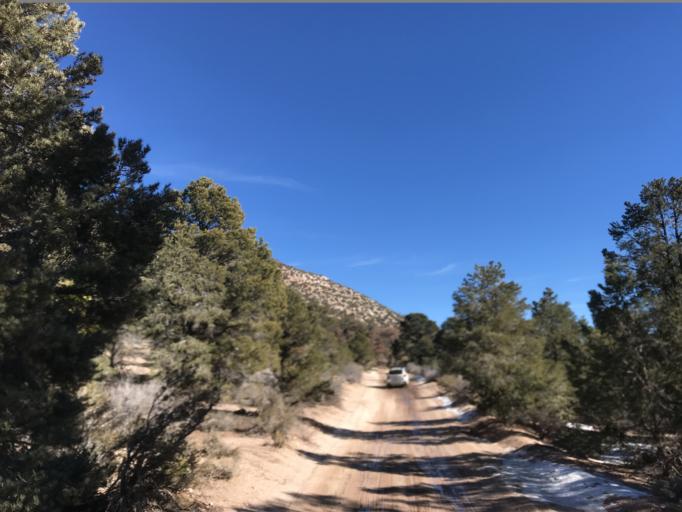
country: US
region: California
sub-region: San Bernardino County
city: Big Bear City
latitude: 34.2416
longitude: -116.6953
